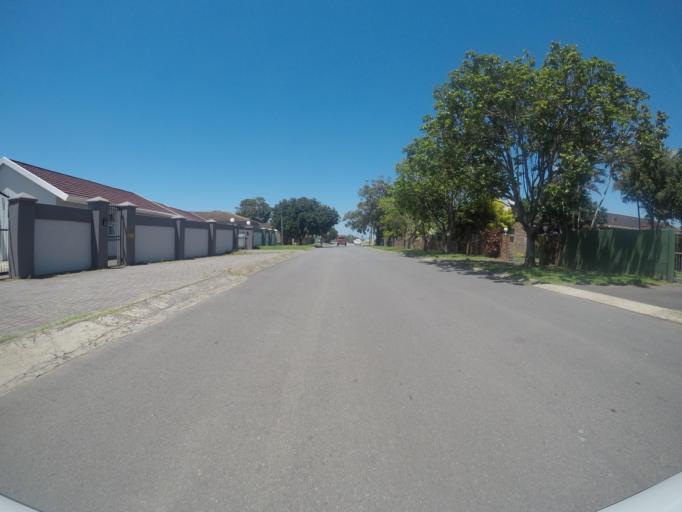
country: ZA
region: Eastern Cape
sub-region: Buffalo City Metropolitan Municipality
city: East London
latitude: -32.9334
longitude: 27.9932
